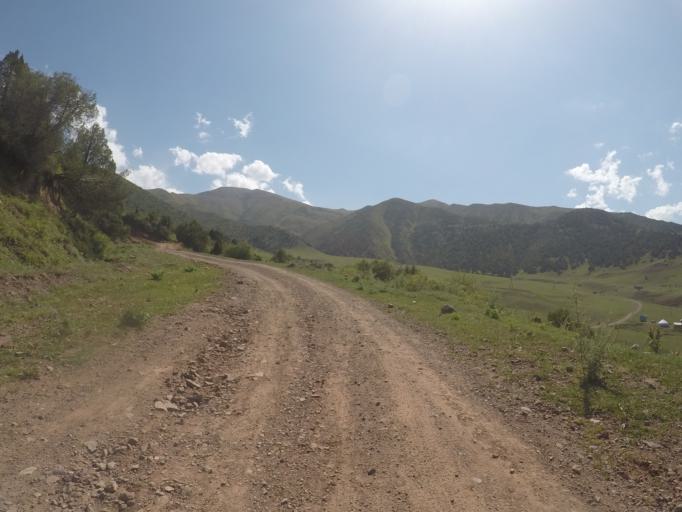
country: KG
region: Chuy
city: Bishkek
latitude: 42.6479
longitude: 74.5773
